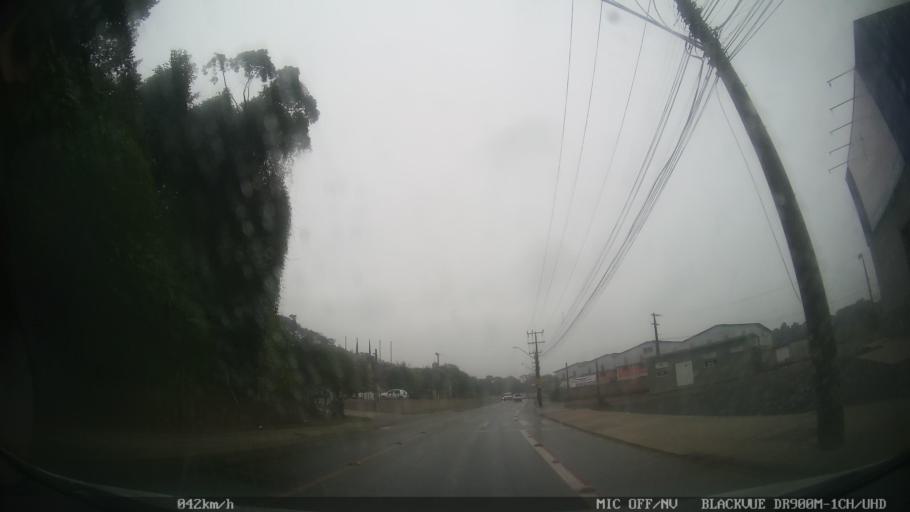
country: BR
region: Santa Catarina
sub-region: Joinville
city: Joinville
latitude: -26.2316
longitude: -48.8184
